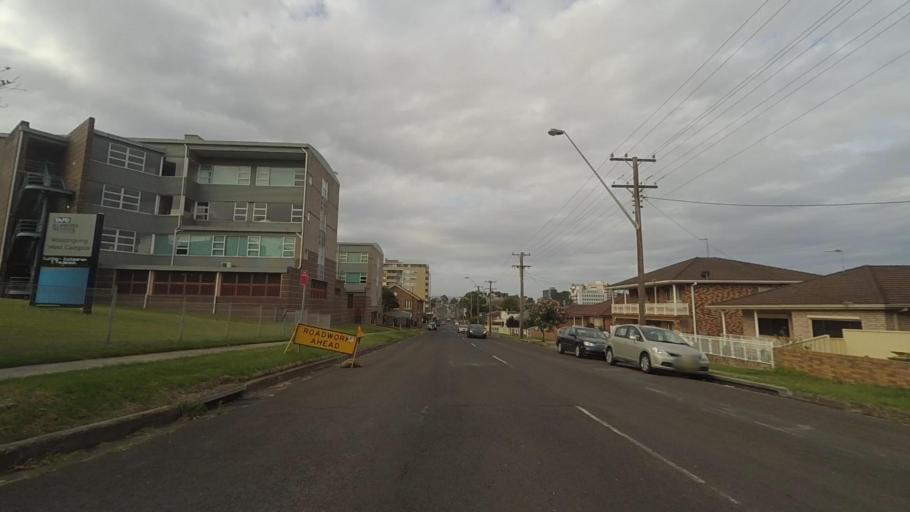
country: AU
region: New South Wales
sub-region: Wollongong
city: Wollongong
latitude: -34.4302
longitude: 150.8864
